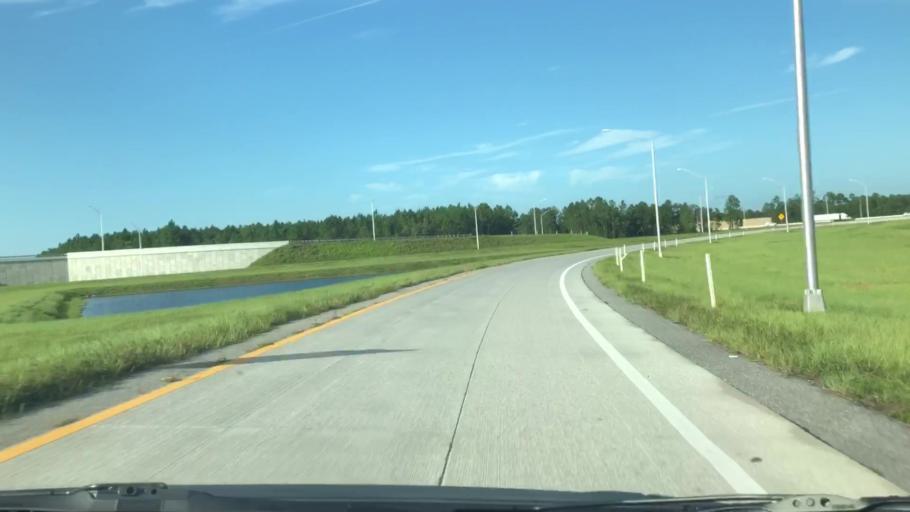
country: US
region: Florida
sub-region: Saint Johns County
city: Fruit Cove
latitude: 30.1206
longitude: -81.5138
